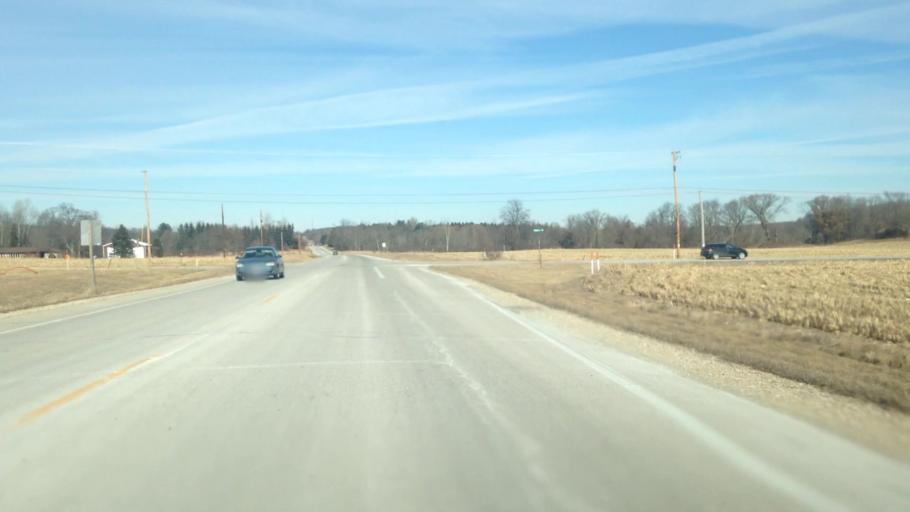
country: US
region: Wisconsin
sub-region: Washington County
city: Slinger
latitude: 43.2803
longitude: -88.2612
